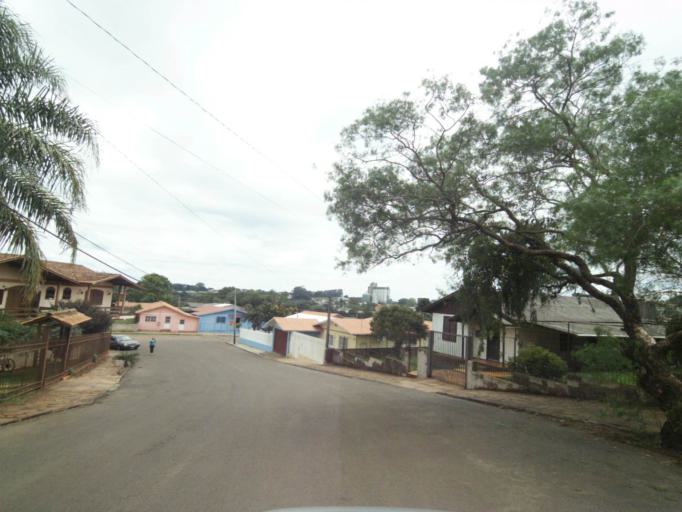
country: BR
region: Rio Grande do Sul
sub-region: Lagoa Vermelha
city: Lagoa Vermelha
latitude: -28.2136
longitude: -51.5351
